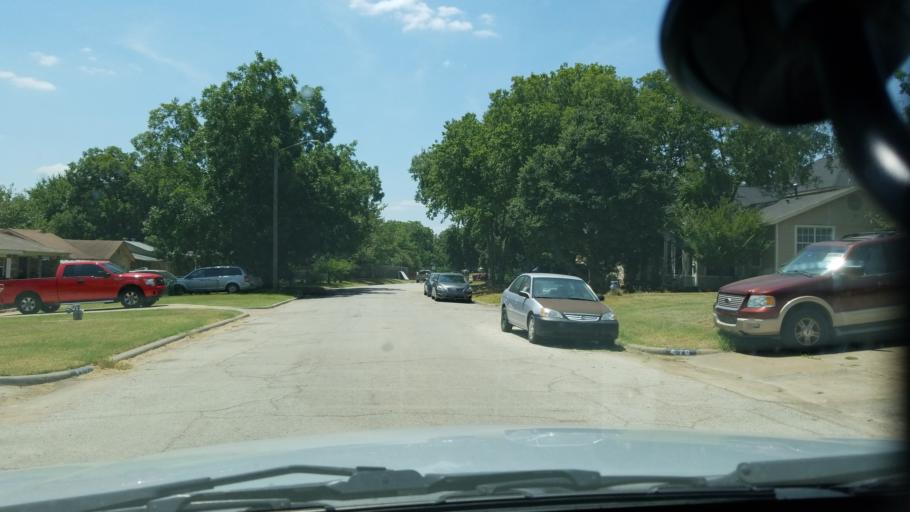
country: US
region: Texas
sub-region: Dallas County
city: Grand Prairie
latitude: 32.7541
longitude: -96.9571
